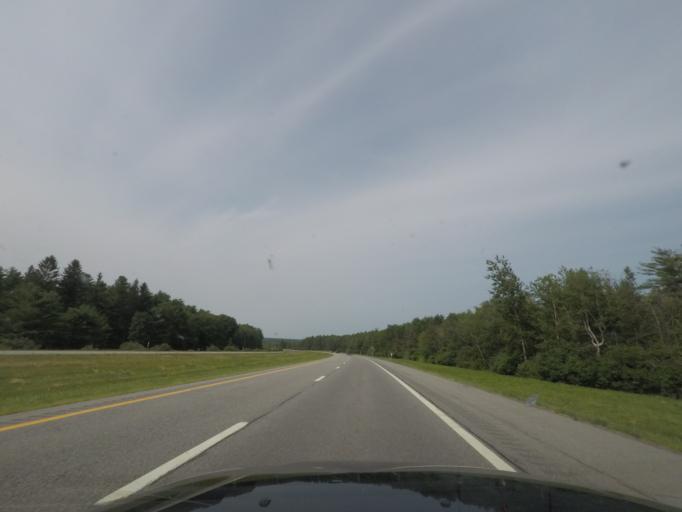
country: US
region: New York
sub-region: Essex County
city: Keeseville
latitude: 44.4576
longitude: -73.4862
